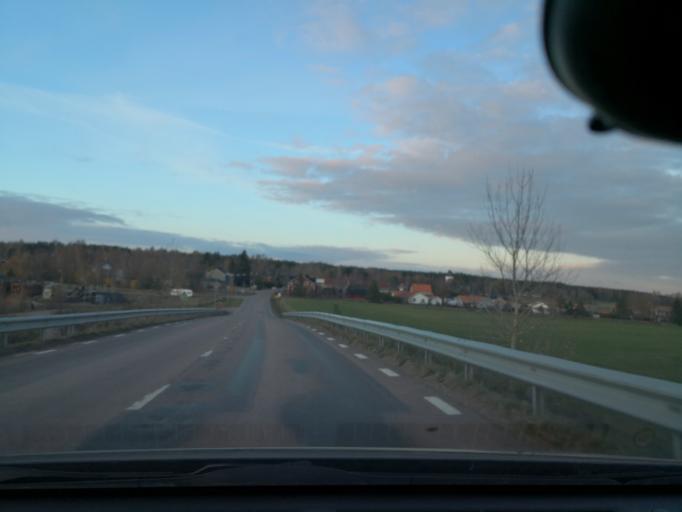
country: SE
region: Vaestmanland
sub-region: Vasteras
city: Tillberga
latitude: 59.6707
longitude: 16.7243
